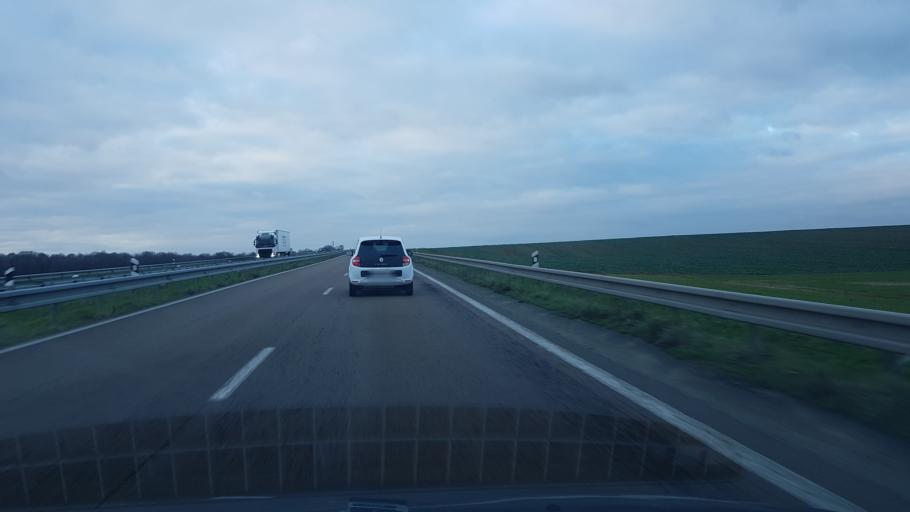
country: FR
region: Champagne-Ardenne
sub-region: Departement de la Marne
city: Sezanne
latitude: 48.7285
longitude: 3.6671
